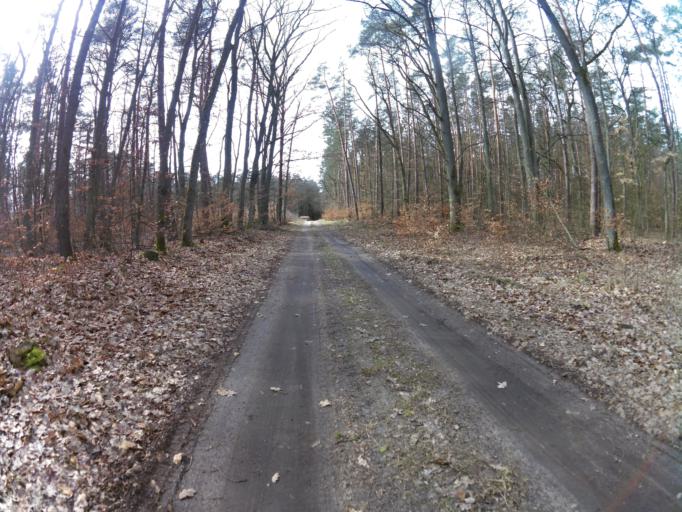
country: PL
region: West Pomeranian Voivodeship
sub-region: Powiat mysliborski
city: Mysliborz
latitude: 52.8604
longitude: 14.8408
